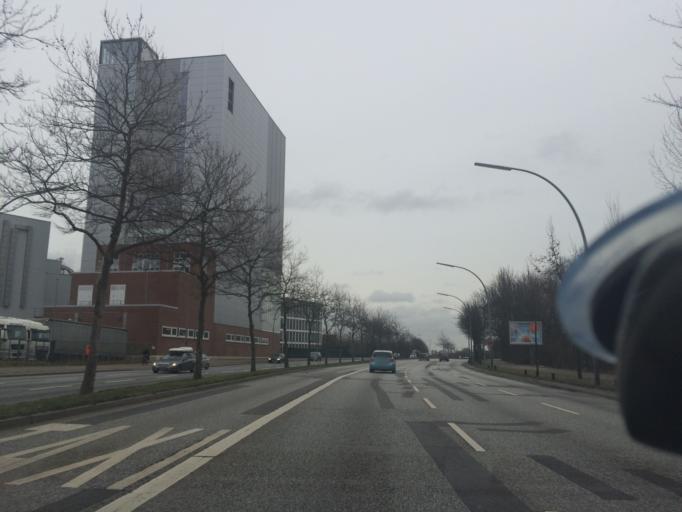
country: DE
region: Hamburg
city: Hammerbrook
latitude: 53.5422
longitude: 10.0272
